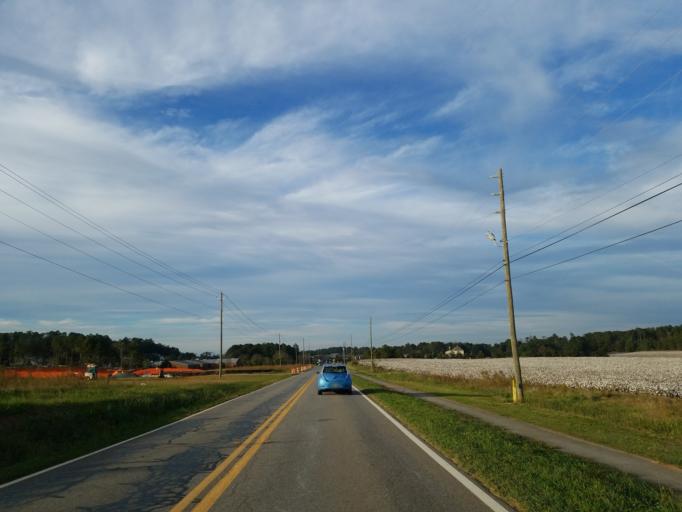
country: US
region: Georgia
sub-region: Bartow County
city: Cartersville
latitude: 34.1311
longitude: -84.8205
